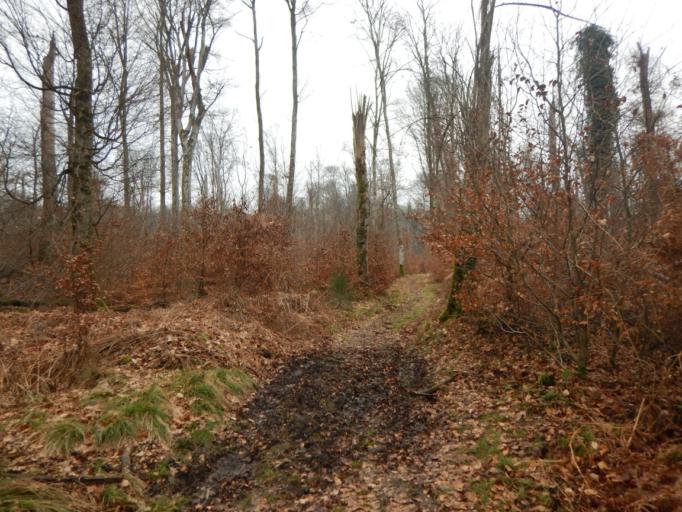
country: LU
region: Luxembourg
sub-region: Canton de Capellen
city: Koerich
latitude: 49.6809
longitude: 5.9546
